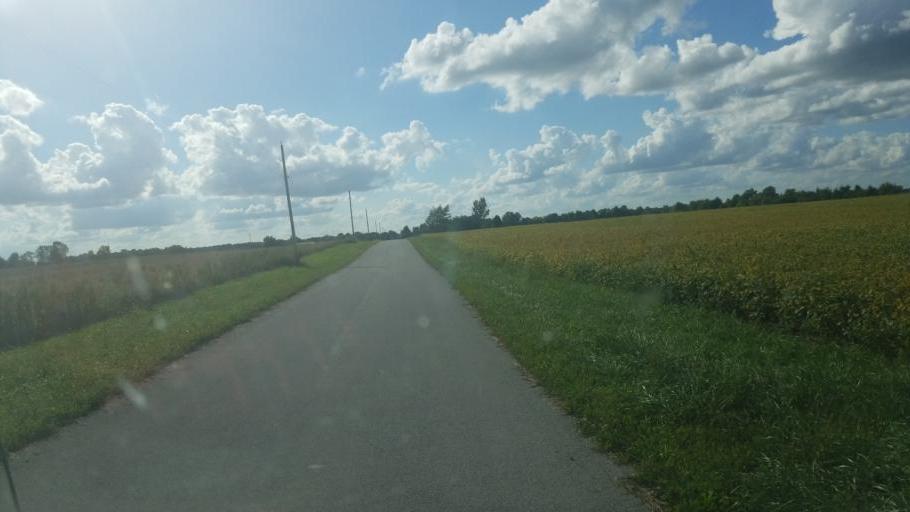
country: US
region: Ohio
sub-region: Hardin County
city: Ada
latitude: 40.7184
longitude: -83.7262
